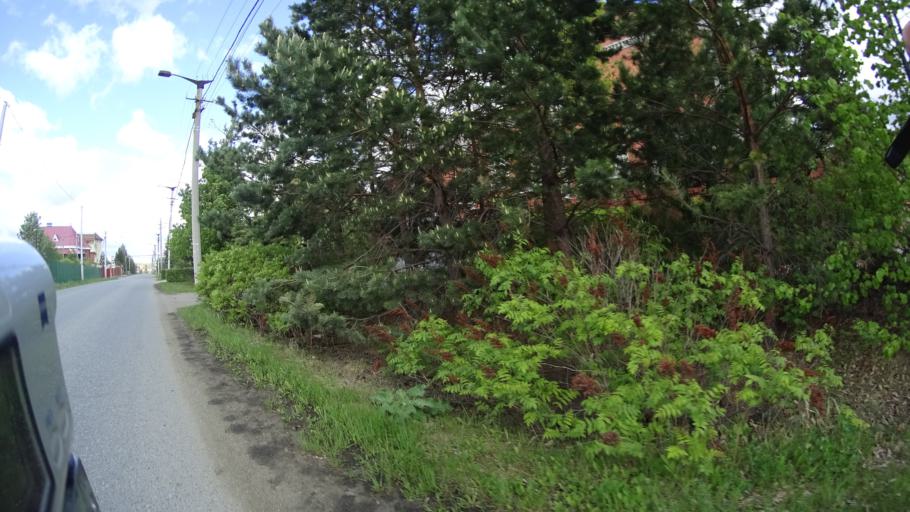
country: RU
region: Chelyabinsk
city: Sargazy
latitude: 55.1444
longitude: 61.2321
